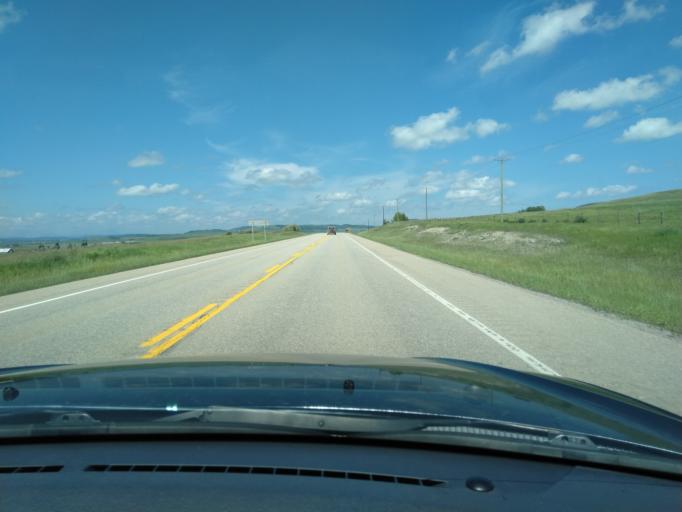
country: CA
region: Alberta
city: Cochrane
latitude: 51.2176
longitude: -114.5382
